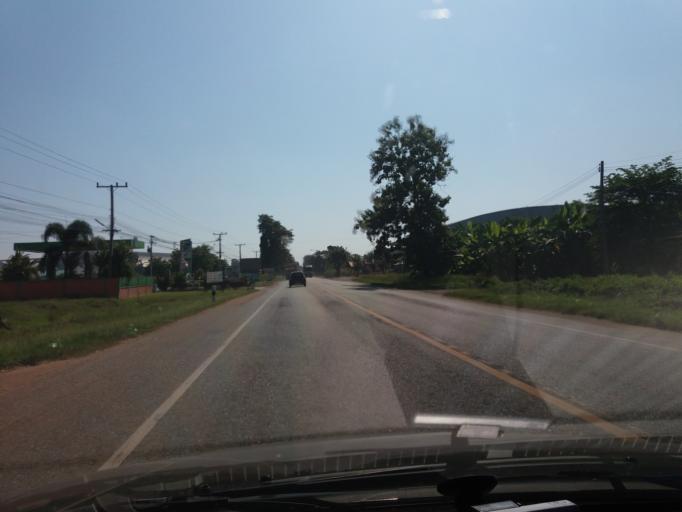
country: TH
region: Kamphaeng Phet
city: Khlong Khlung
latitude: 16.1772
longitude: 99.7887
